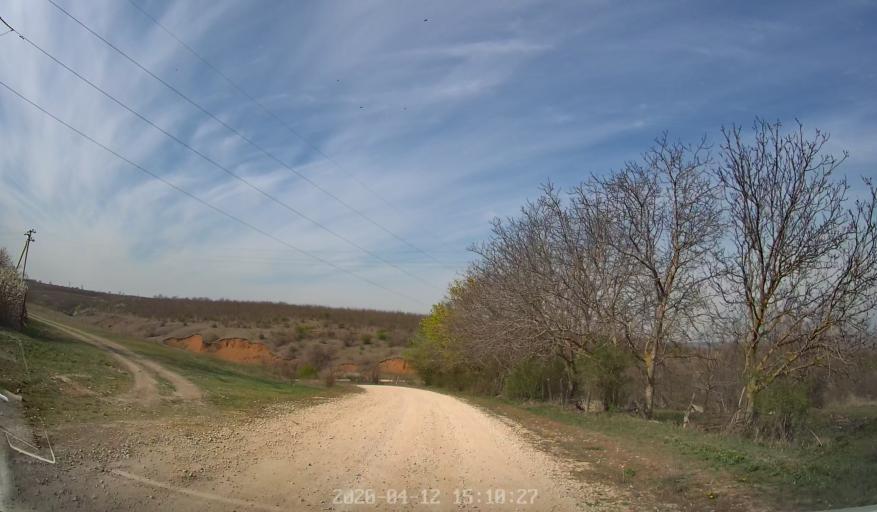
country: MD
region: Telenesti
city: Cocieri
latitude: 47.3235
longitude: 29.0679
